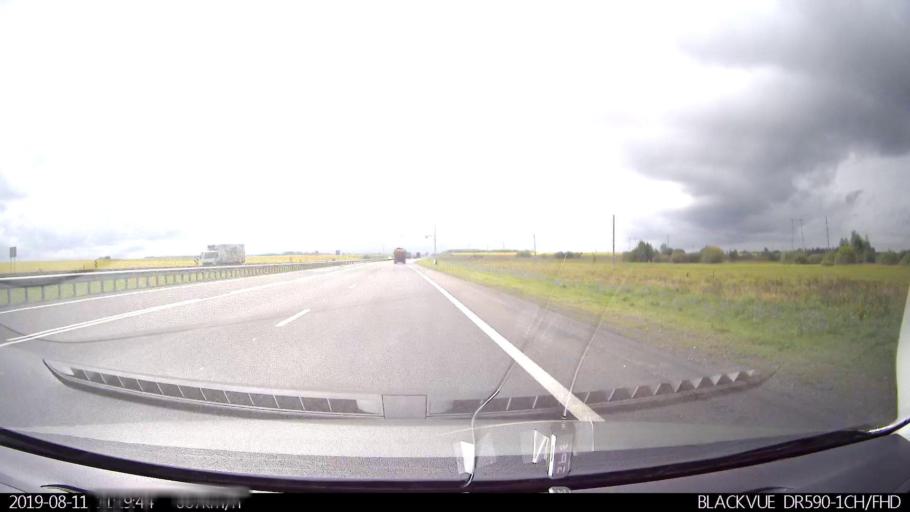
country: RU
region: Ulyanovsk
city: Novoul'yanovsk
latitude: 54.1655
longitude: 48.2646
